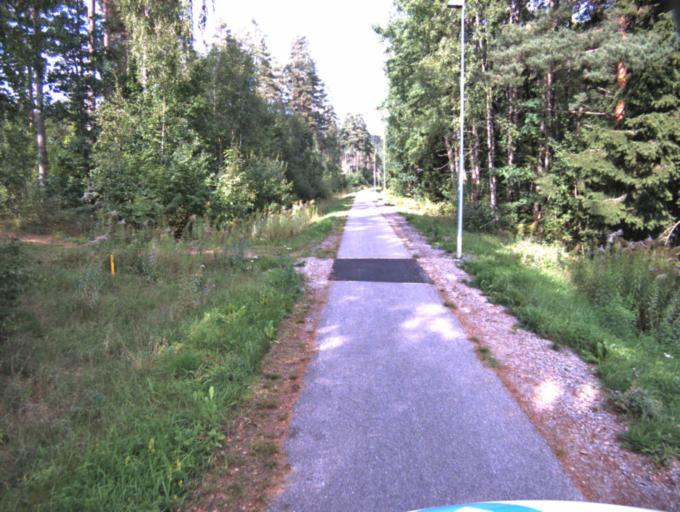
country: SE
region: Vaestra Goetaland
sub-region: Ulricehamns Kommun
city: Ulricehamn
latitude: 57.8161
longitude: 13.4119
